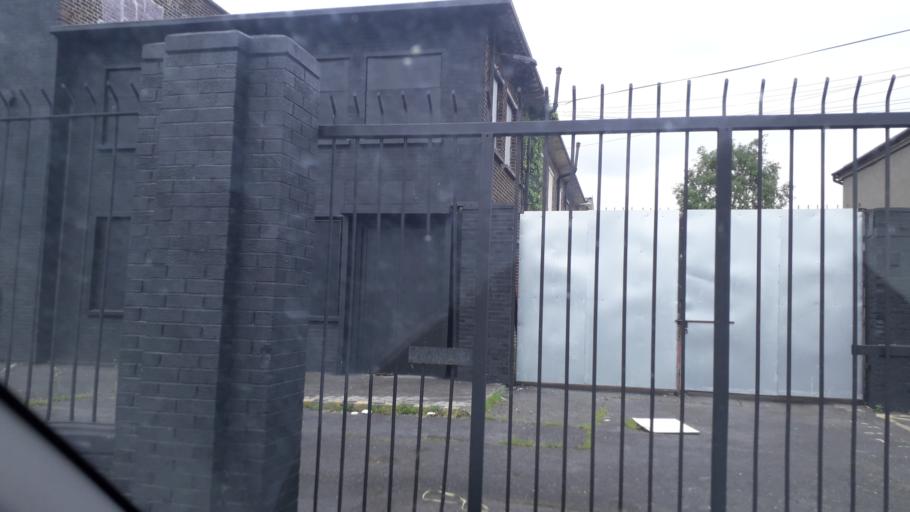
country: IE
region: Leinster
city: Crumlin
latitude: 53.3355
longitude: -6.3347
